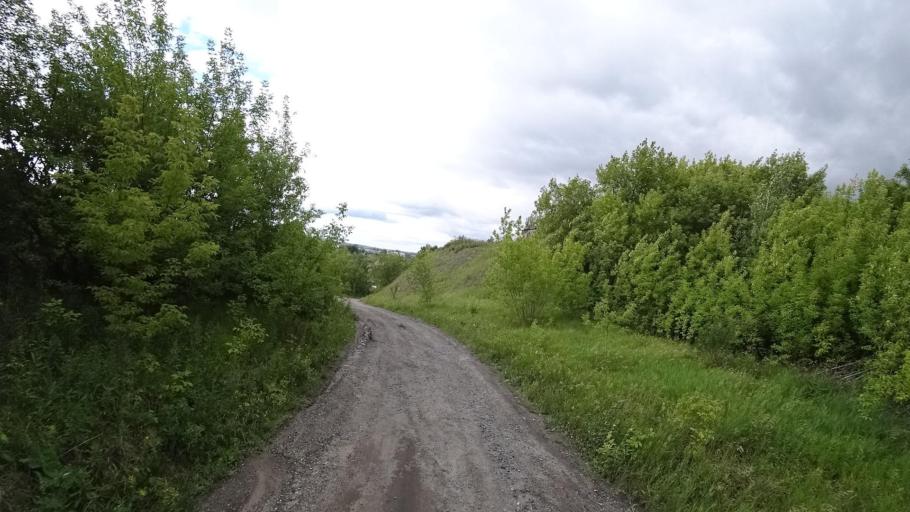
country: RU
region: Sverdlovsk
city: Kamyshlov
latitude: 56.8557
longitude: 62.7187
